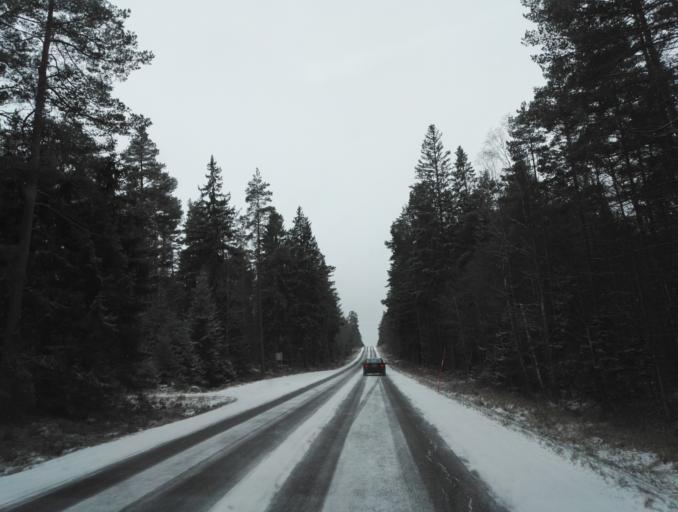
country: SE
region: Kronoberg
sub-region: Lessebo Kommun
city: Lessebo
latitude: 56.7640
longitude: 15.2908
